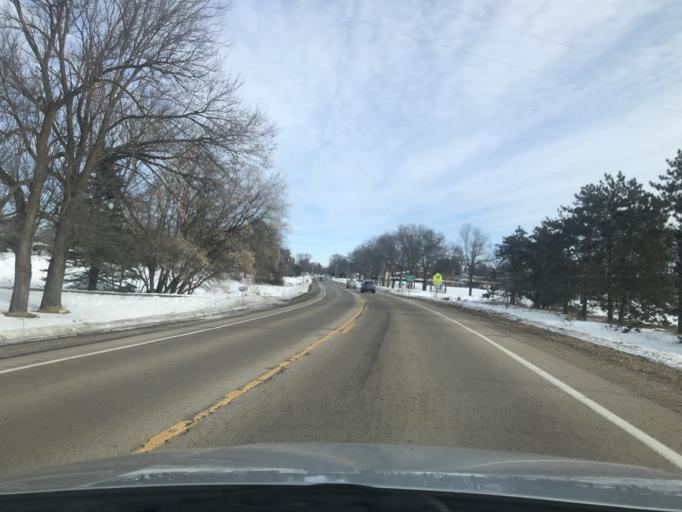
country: US
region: Wisconsin
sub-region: Oconto County
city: Gillett
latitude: 44.8861
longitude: -88.3195
